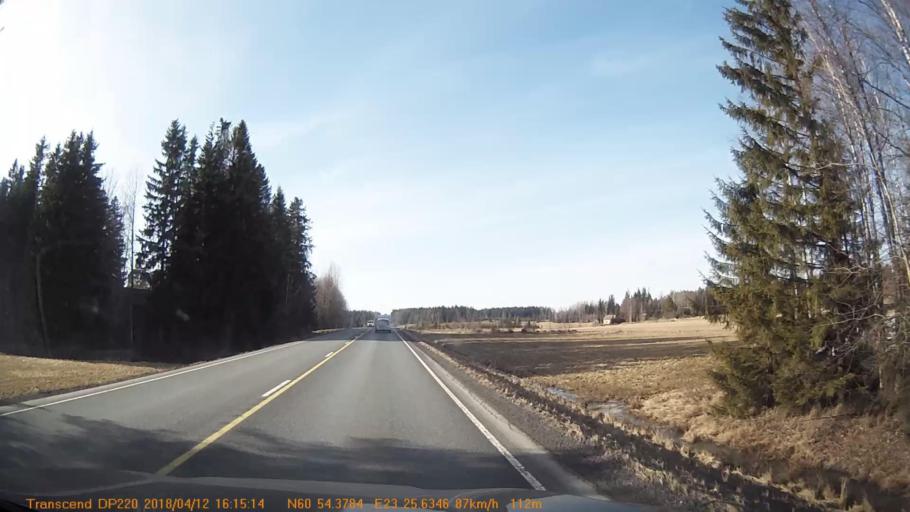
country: FI
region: Haeme
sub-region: Forssa
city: Humppila
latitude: 60.9065
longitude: 23.4269
